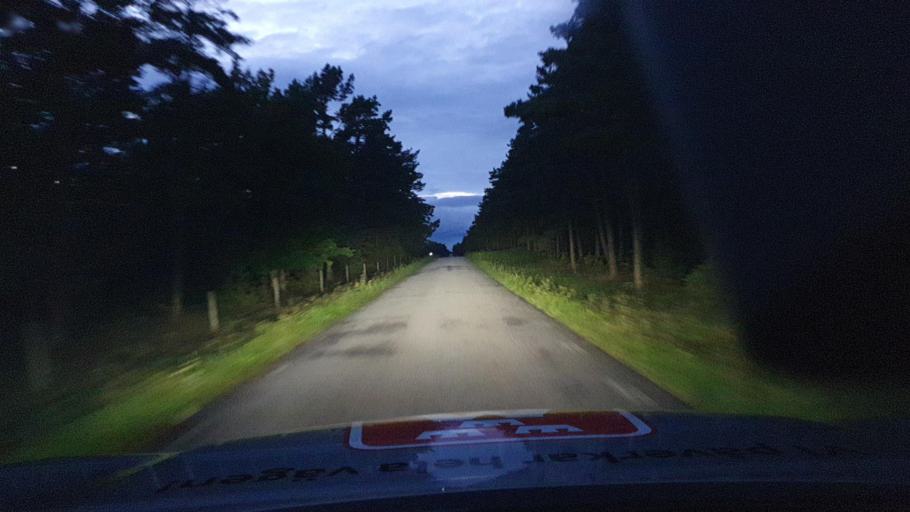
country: SE
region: Gotland
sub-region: Gotland
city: Slite
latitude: 57.7857
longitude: 18.6399
